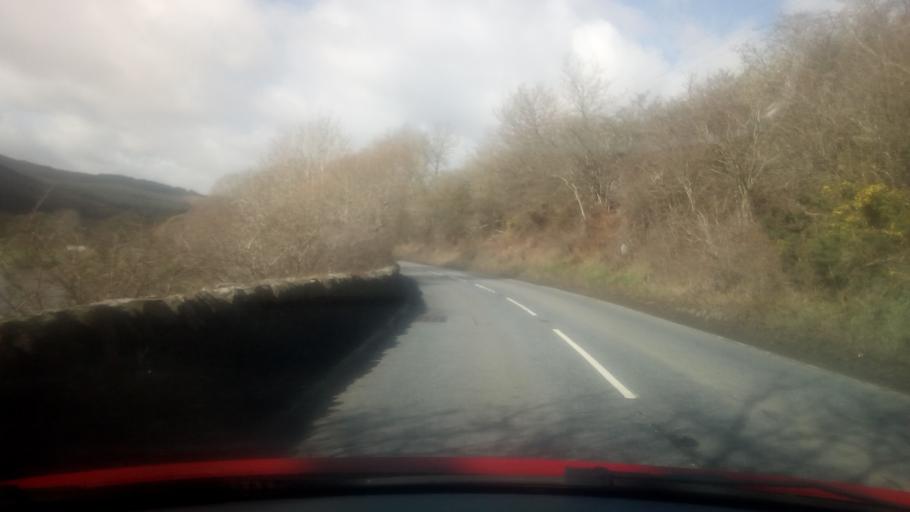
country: GB
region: Scotland
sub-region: The Scottish Borders
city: Selkirk
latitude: 55.6174
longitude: -2.9251
